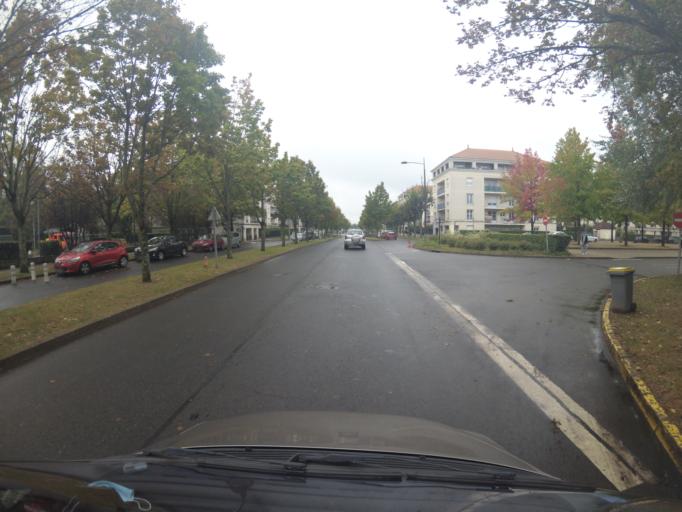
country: FR
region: Ile-de-France
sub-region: Departement de Seine-et-Marne
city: Conches-sur-Gondoire
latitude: 48.8404
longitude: 2.7210
